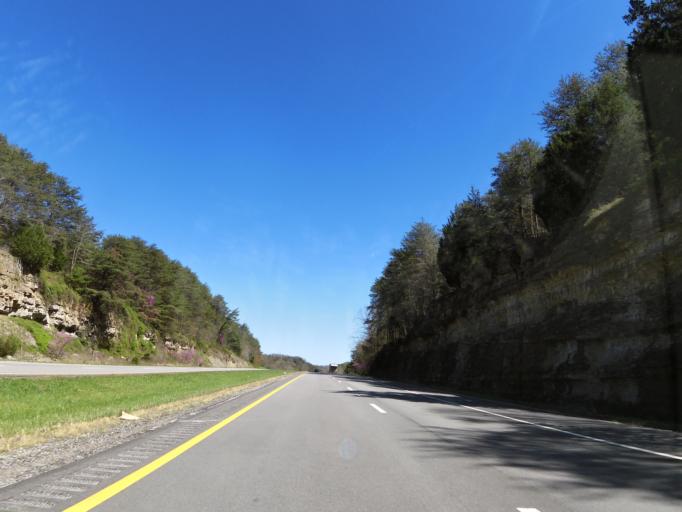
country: US
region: Kentucky
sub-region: Pulaski County
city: Somerset
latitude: 37.0990
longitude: -84.8414
